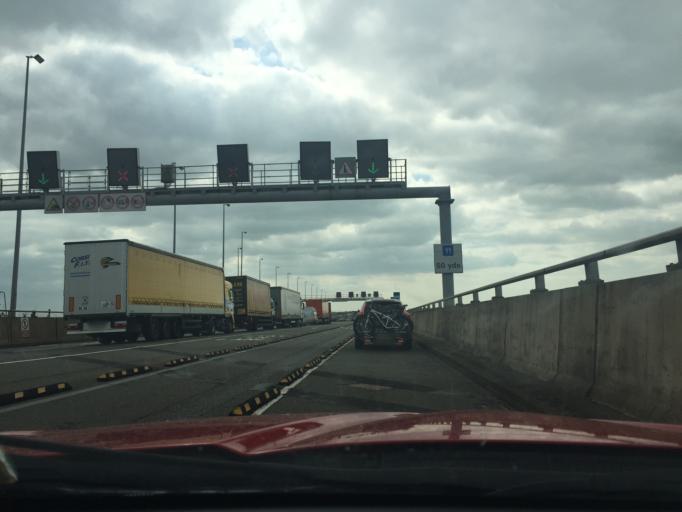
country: GB
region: England
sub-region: Kent
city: Hawkinge
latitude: 51.0969
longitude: 1.1284
